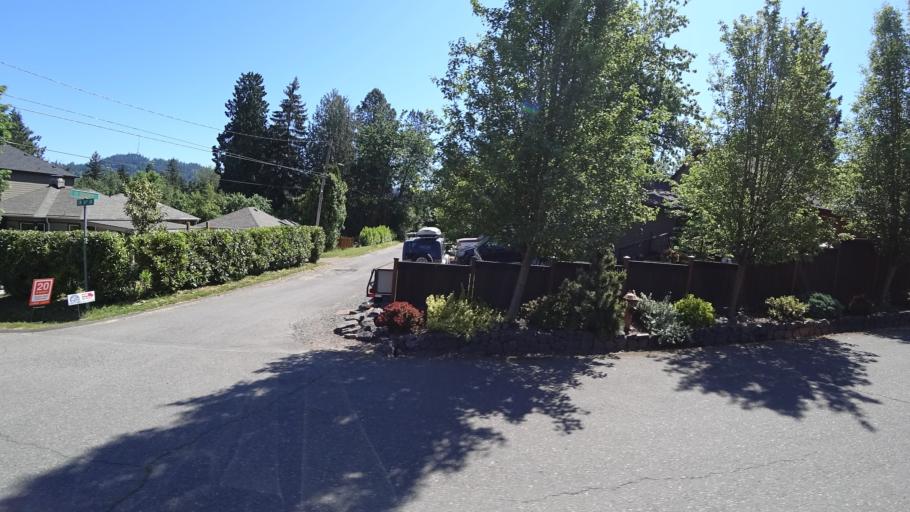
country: US
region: Oregon
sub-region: Washington County
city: Raleigh Hills
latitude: 45.4857
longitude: -122.7284
